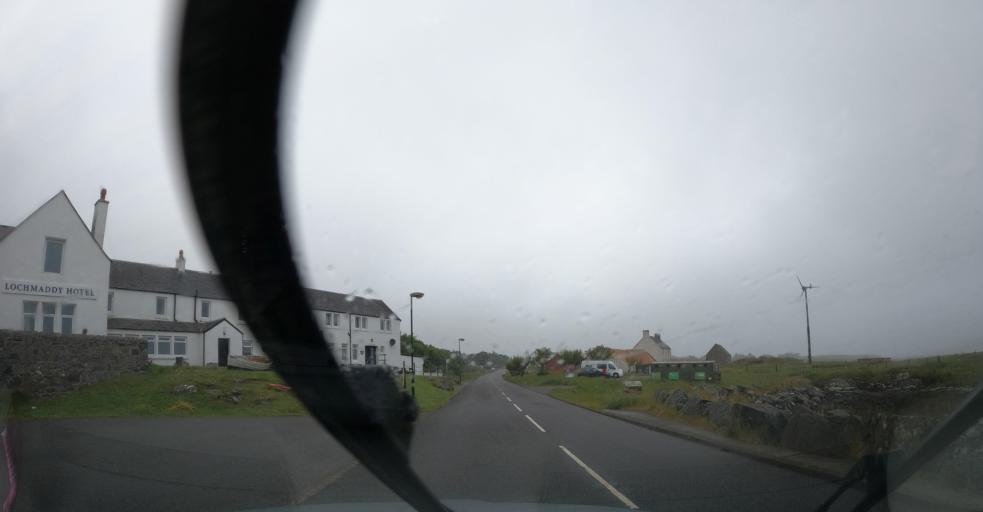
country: GB
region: Scotland
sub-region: Eilean Siar
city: Isle of North Uist
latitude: 57.5979
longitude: -7.1585
